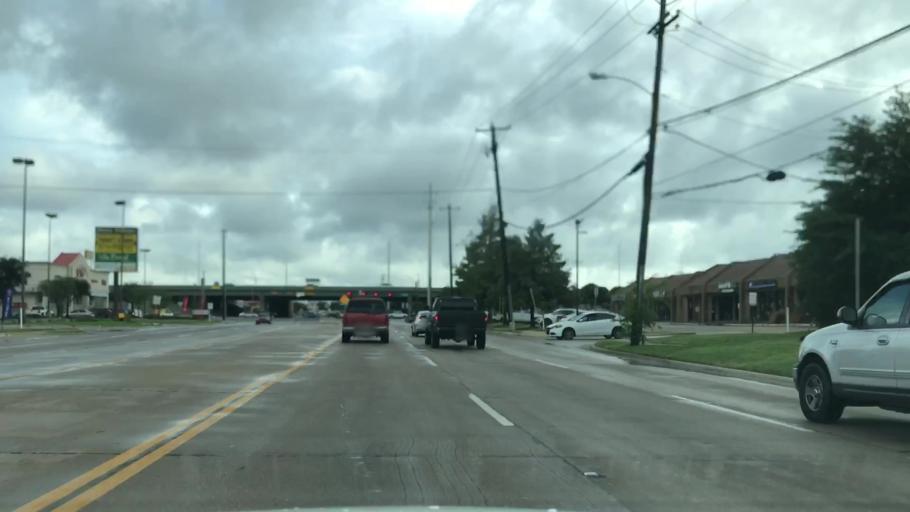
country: US
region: Texas
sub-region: Dallas County
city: Irving
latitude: 32.8395
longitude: -96.9766
